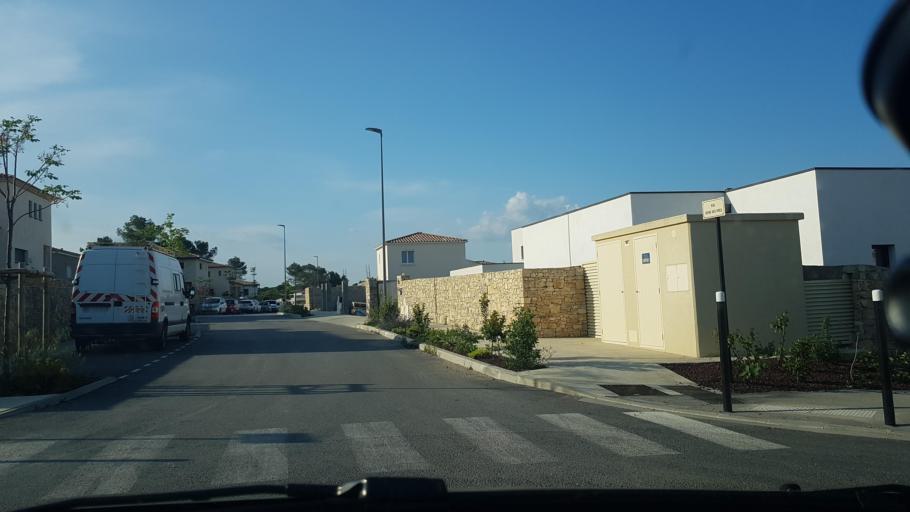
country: FR
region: Languedoc-Roussillon
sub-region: Departement du Gard
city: Caveirac
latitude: 43.8418
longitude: 4.2985
